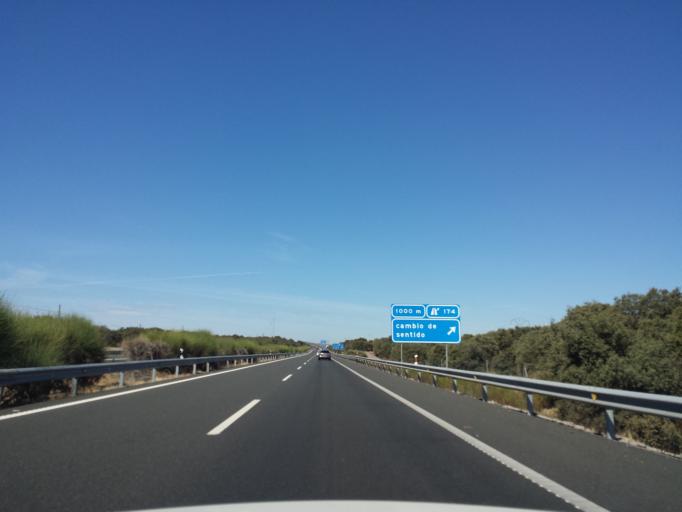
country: ES
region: Extremadura
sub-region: Provincia de Caceres
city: Peraleda de la Mata
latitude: 39.8901
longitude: -5.4488
